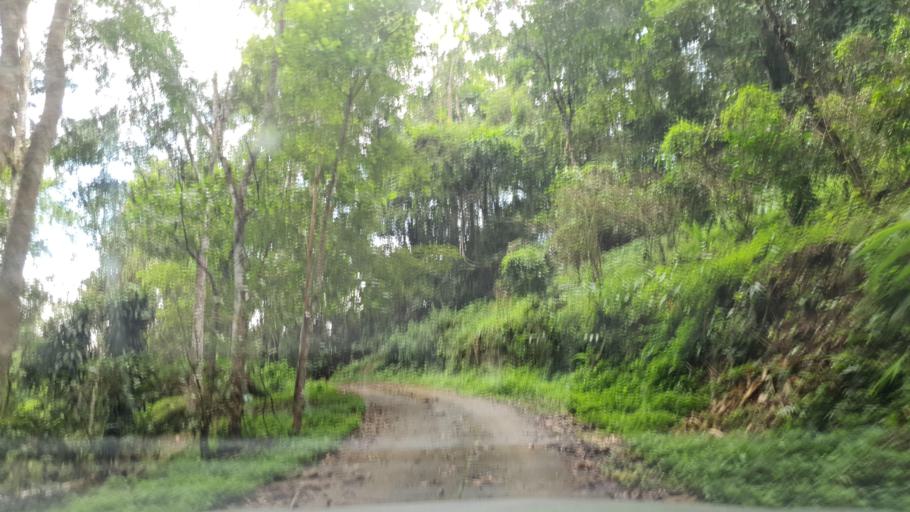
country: TH
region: Chiang Mai
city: Mae On
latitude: 18.9256
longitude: 99.3096
